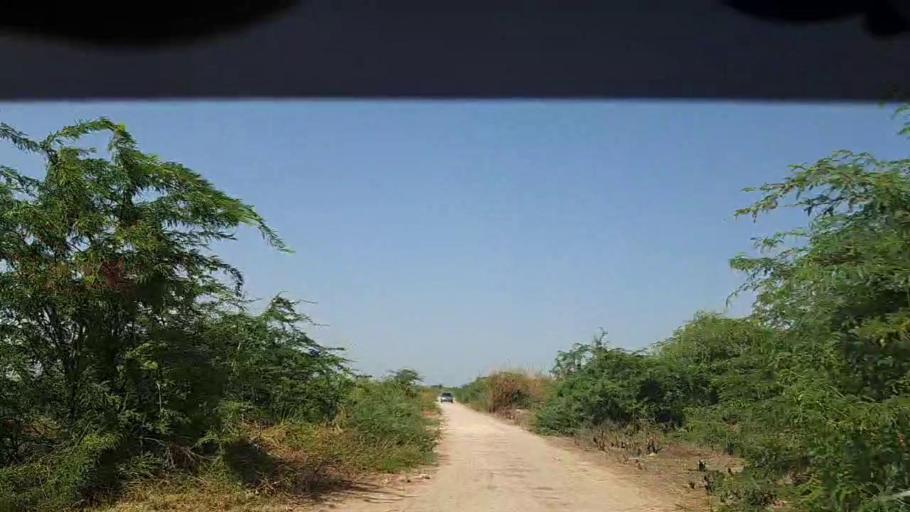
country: PK
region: Sindh
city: Badin
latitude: 24.4651
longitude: 68.7797
